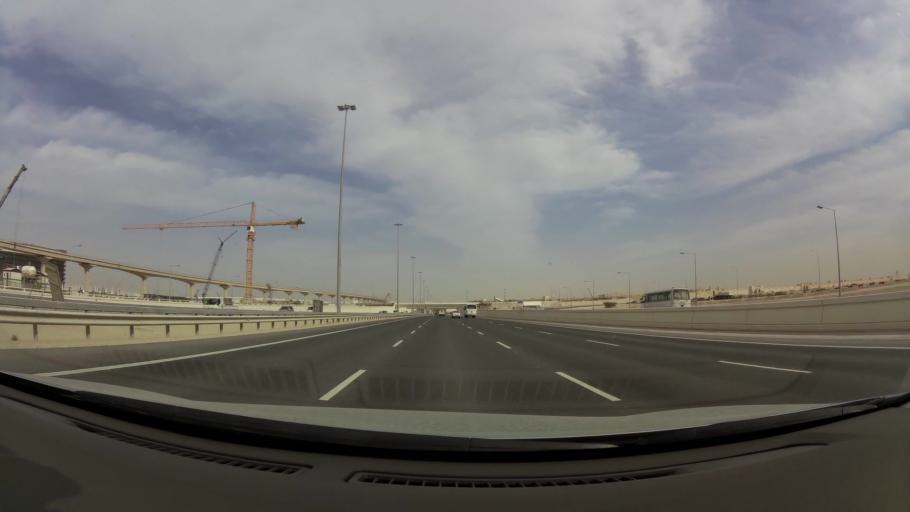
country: QA
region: Baladiyat ar Rayyan
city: Ar Rayyan
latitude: 25.3228
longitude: 51.3474
